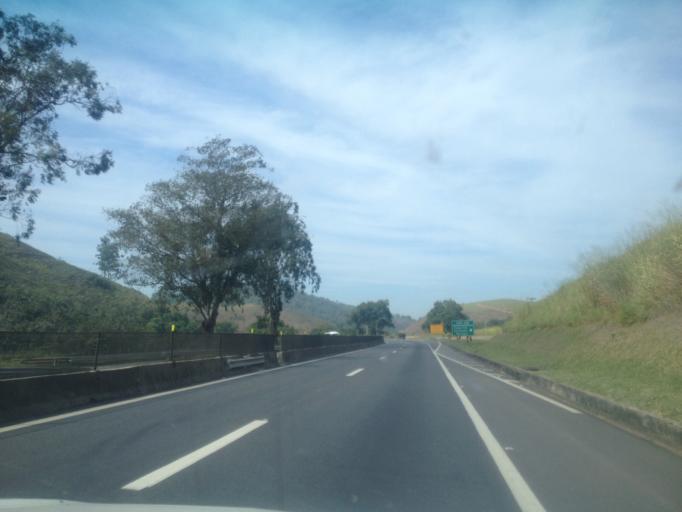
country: BR
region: Rio de Janeiro
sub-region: Pirai
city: Pirai
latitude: -22.6620
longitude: -43.8869
